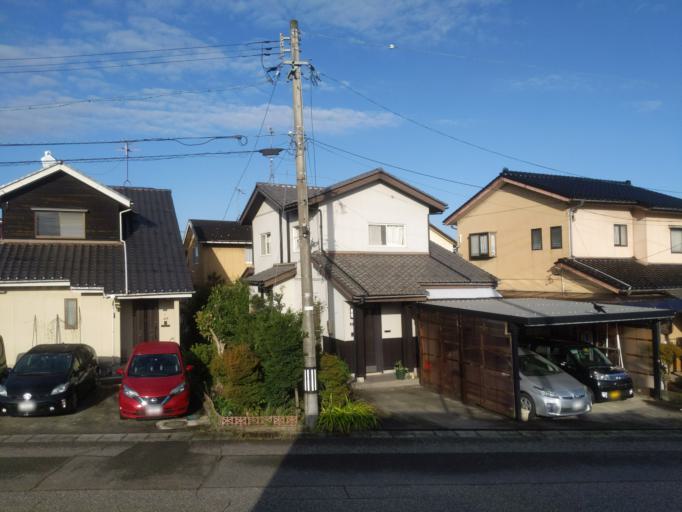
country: JP
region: Toyama
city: Kamiichi
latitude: 36.6678
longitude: 137.3144
